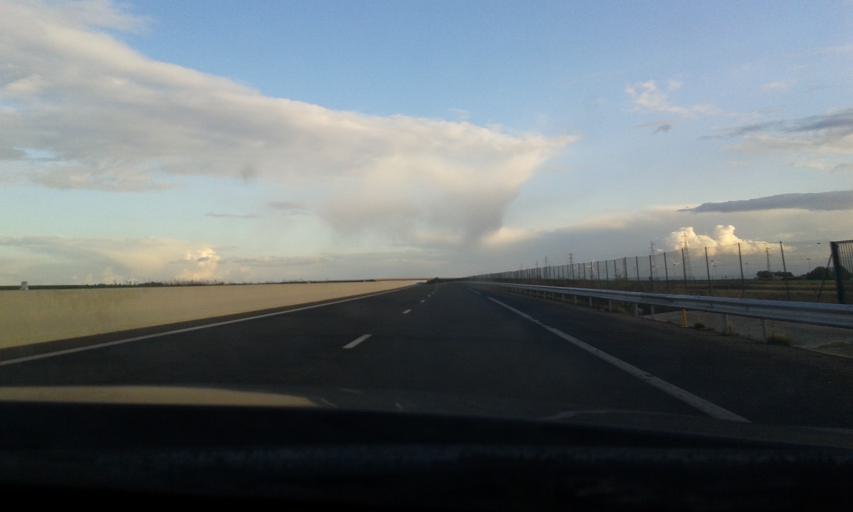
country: FR
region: Centre
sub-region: Departement d'Eure-et-Loir
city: Sours
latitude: 48.3618
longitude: 1.6022
